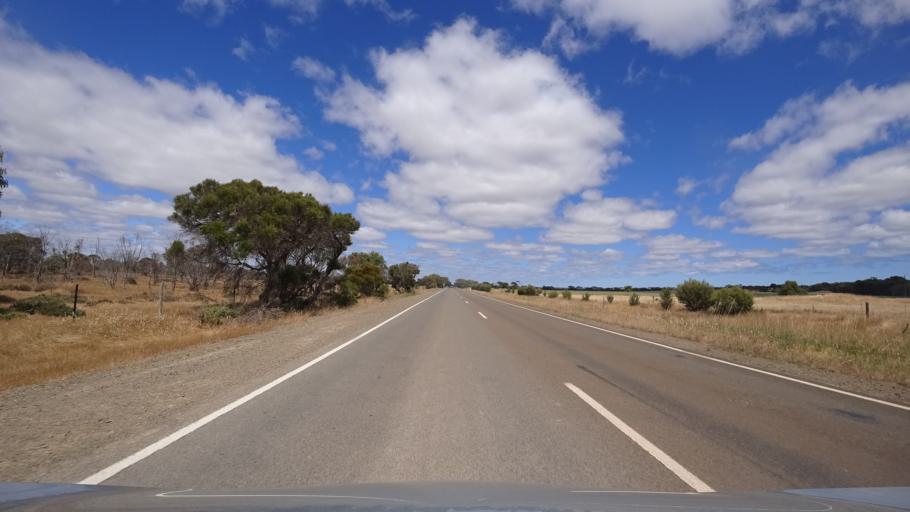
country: AU
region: South Australia
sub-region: Kangaroo Island
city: Kingscote
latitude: -35.6790
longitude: 137.5697
